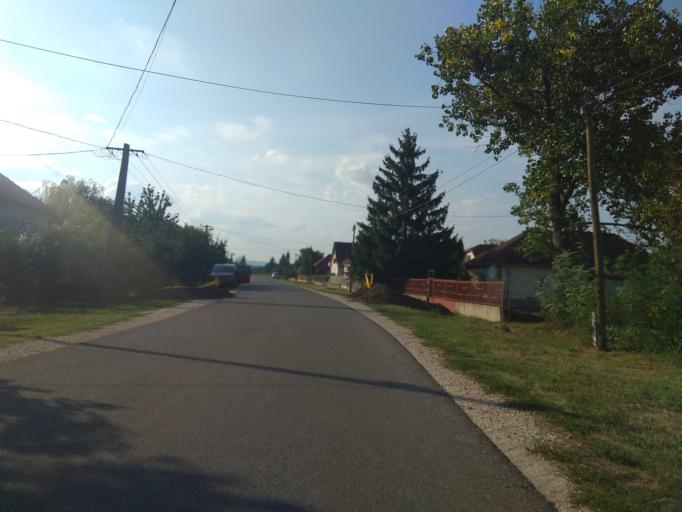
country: HU
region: Borsod-Abauj-Zemplen
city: Emod
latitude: 47.8860
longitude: 20.7694
